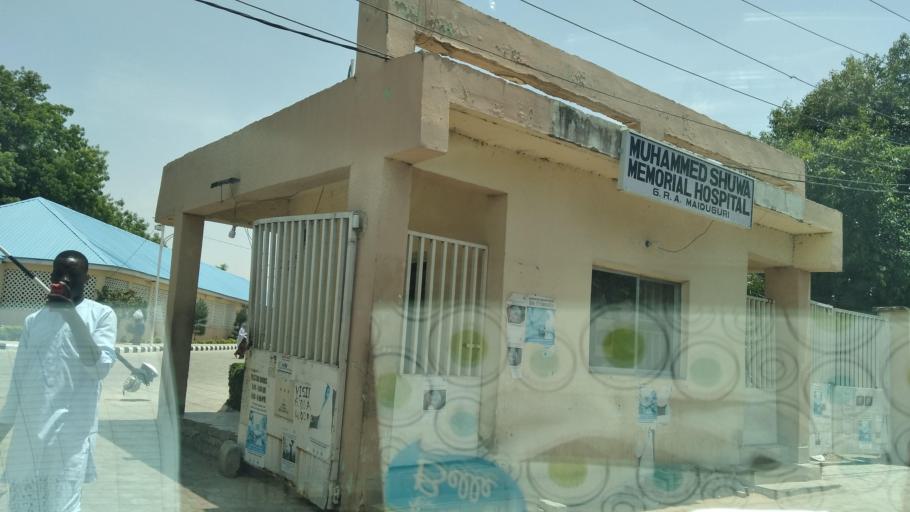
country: NG
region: Borno
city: Maiduguri
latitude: 11.8224
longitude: 13.1484
